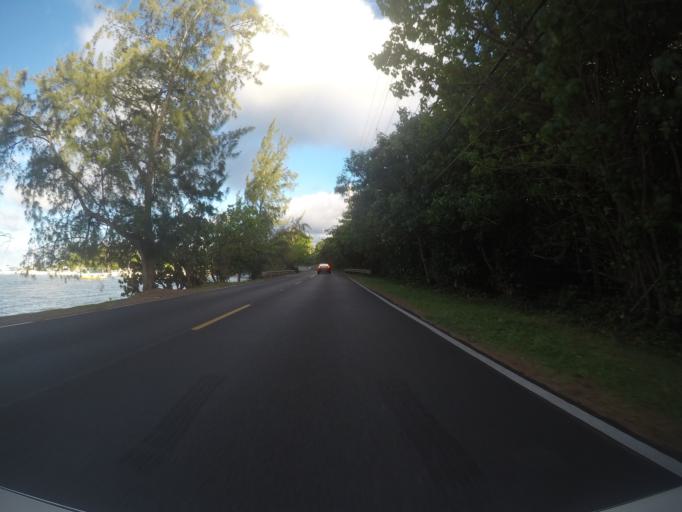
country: US
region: Hawaii
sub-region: Honolulu County
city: He'eia
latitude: 21.4437
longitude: -157.8125
